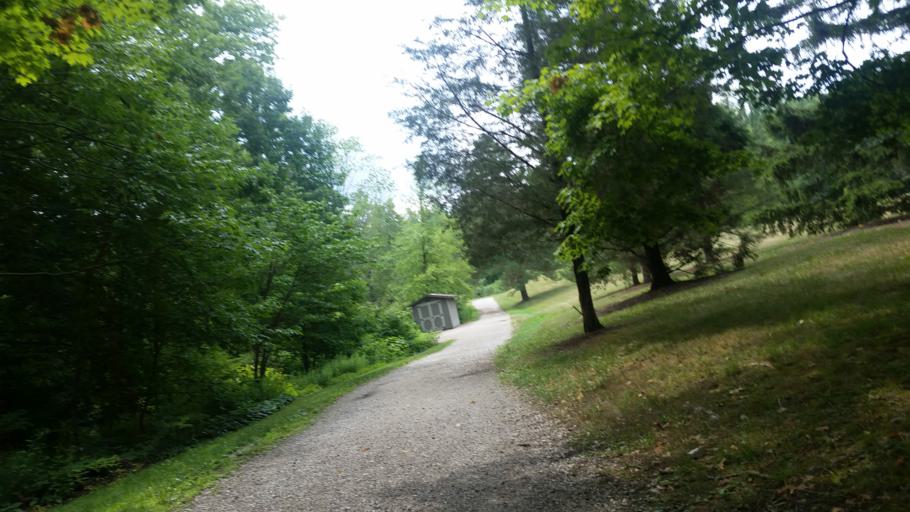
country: US
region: Ohio
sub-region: Lake County
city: Kirtland
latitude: 41.6107
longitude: -81.3030
